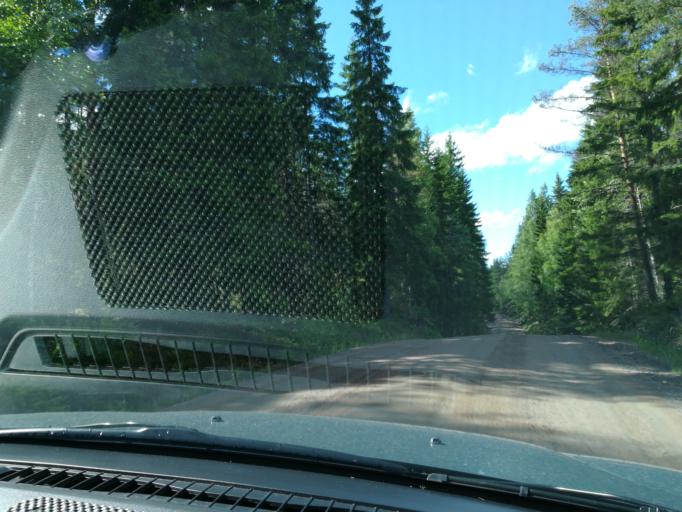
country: FI
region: South Karelia
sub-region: Lappeenranta
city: Savitaipale
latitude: 61.3050
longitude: 27.6361
